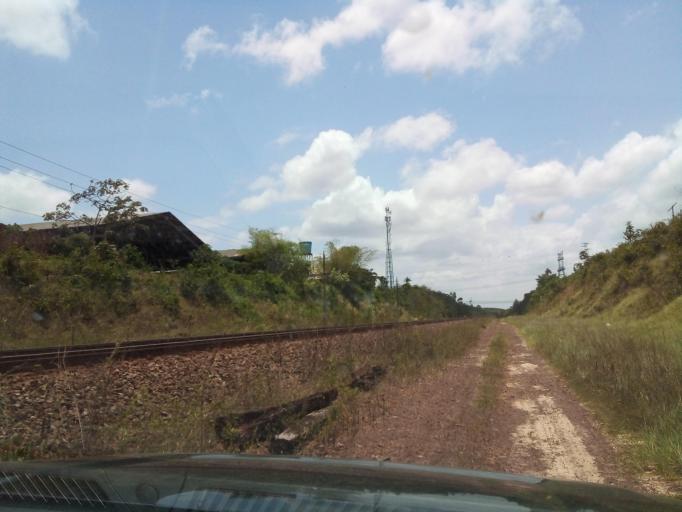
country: BR
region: Maranhao
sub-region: Sao Luis
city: Sao Luis
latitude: -2.7063
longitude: -44.3151
